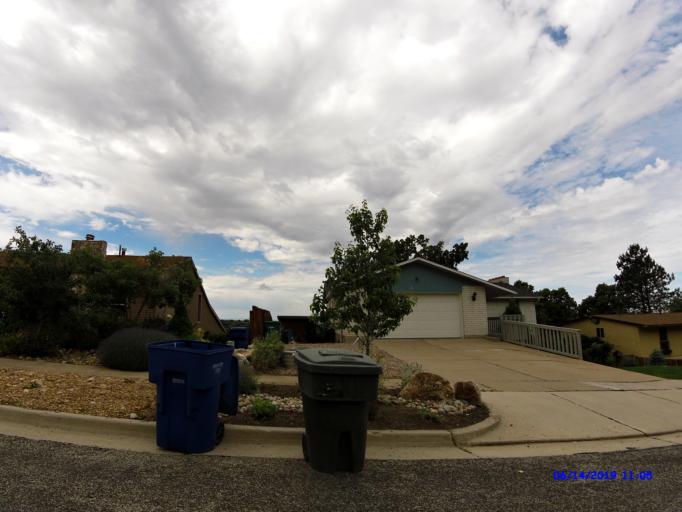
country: US
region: Utah
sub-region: Weber County
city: Ogden
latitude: 41.2434
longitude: -111.9356
